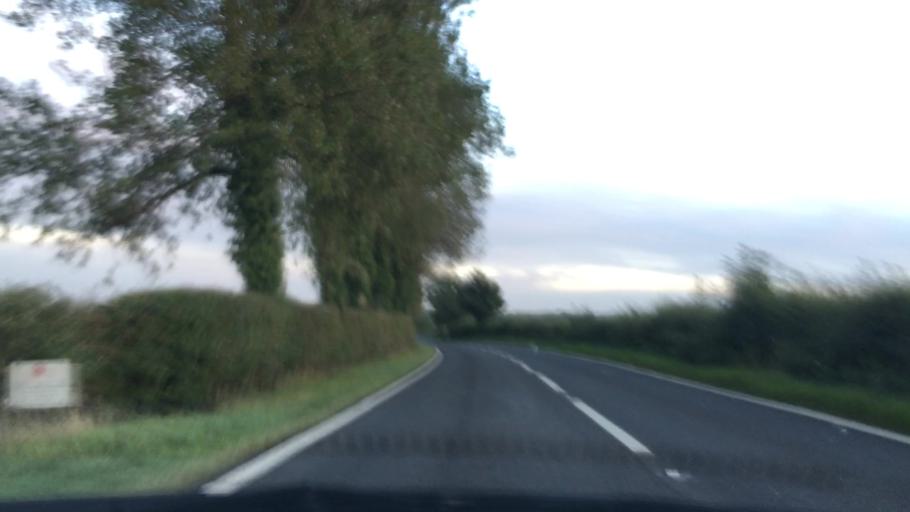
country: GB
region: England
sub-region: North East Lincolnshire
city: Wold Newton
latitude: 53.4604
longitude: -0.0938
